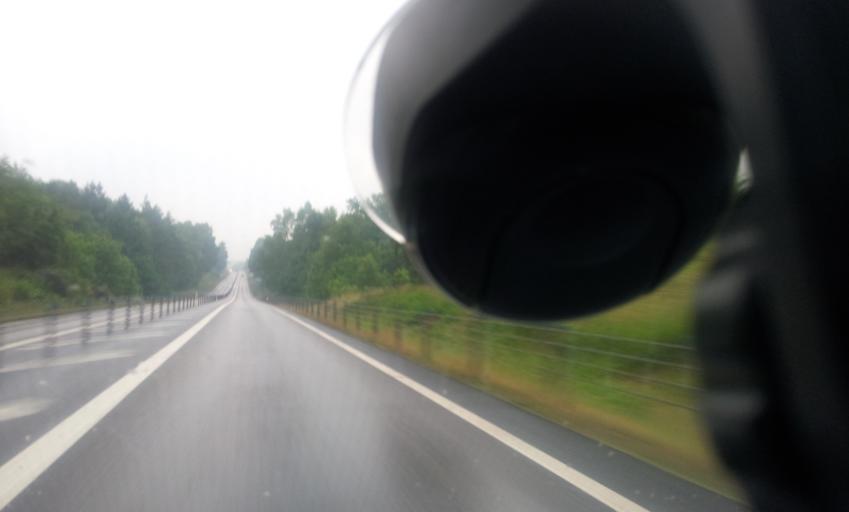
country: SE
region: Kalmar
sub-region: Vasterviks Kommun
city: Gamleby
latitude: 57.8635
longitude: 16.4234
